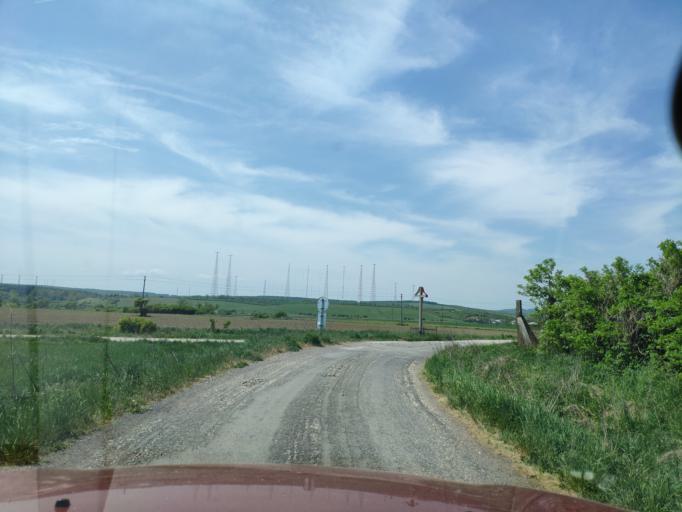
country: SK
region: Banskobystricky
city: Rimavska Sobota
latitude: 48.4152
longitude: 20.1515
